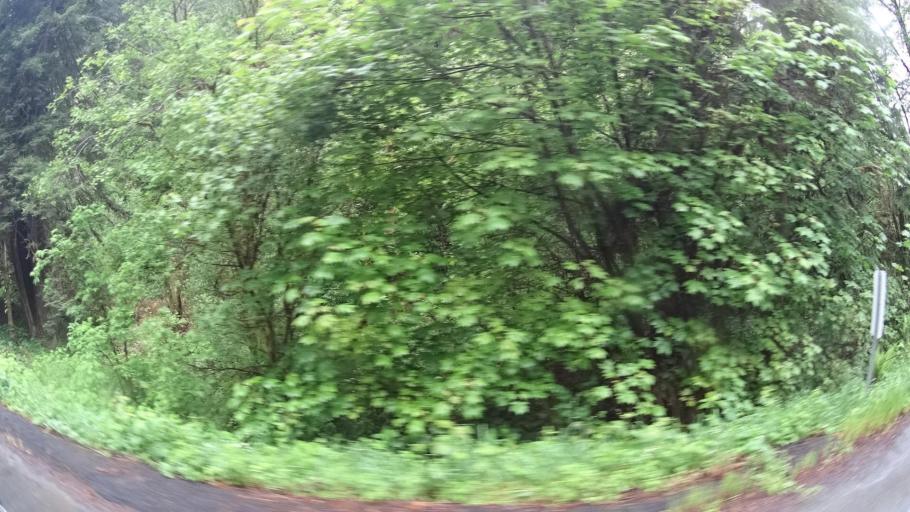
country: US
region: California
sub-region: Humboldt County
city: Bayside
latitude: 40.8142
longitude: -124.0258
